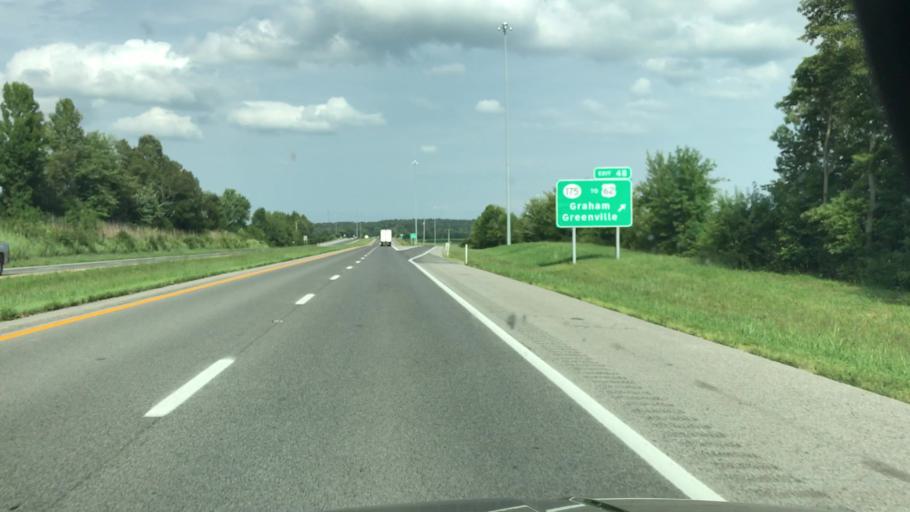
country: US
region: Kentucky
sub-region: Muhlenberg County
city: Greenville
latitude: 37.2329
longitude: -87.2814
